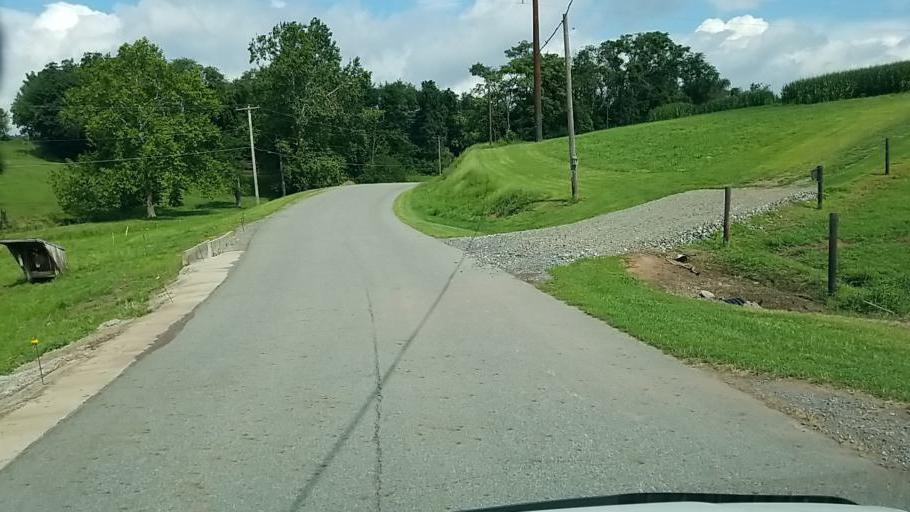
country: US
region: Pennsylvania
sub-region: Dauphin County
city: Millersburg
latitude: 40.5635
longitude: -76.9279
